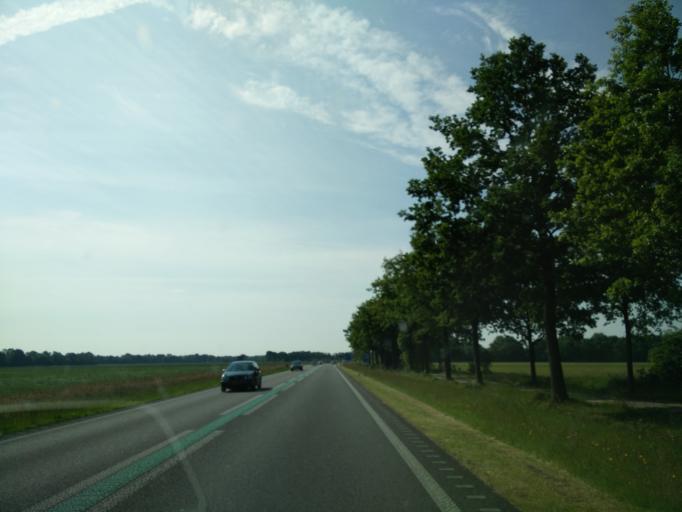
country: NL
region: Drenthe
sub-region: Gemeente Borger-Odoorn
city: Borger
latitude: 52.9808
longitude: 6.7720
